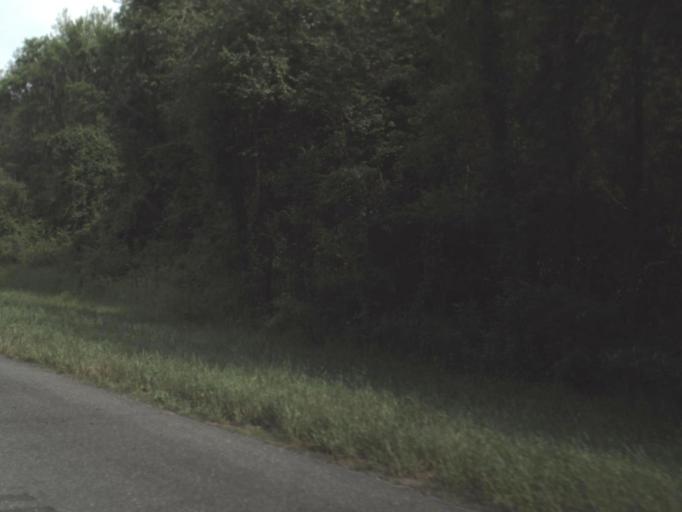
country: US
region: Florida
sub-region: Suwannee County
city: Live Oak
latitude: 30.2996
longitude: -82.9086
